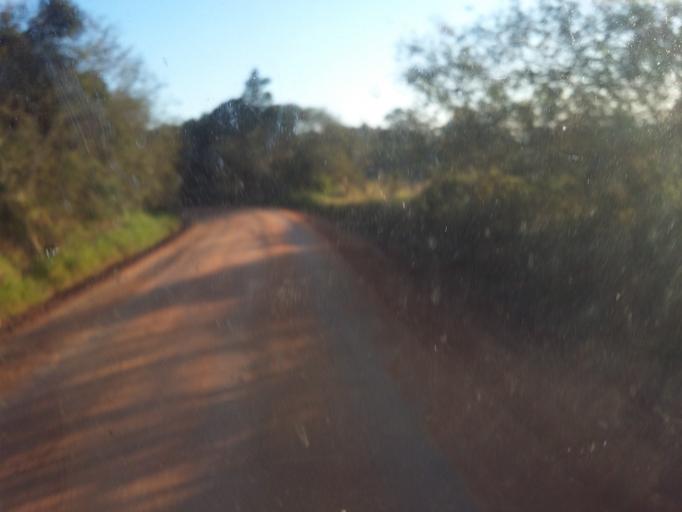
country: BR
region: Rio Grande do Sul
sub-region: Camaqua
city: Camaqua
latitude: -30.7780
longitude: -51.7924
